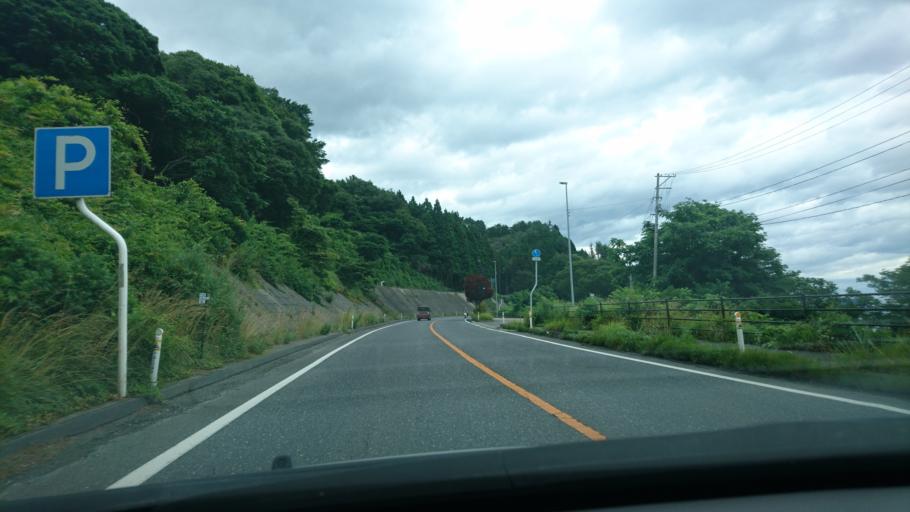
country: JP
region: Iwate
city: Otsuchi
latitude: 39.3873
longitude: 141.9386
